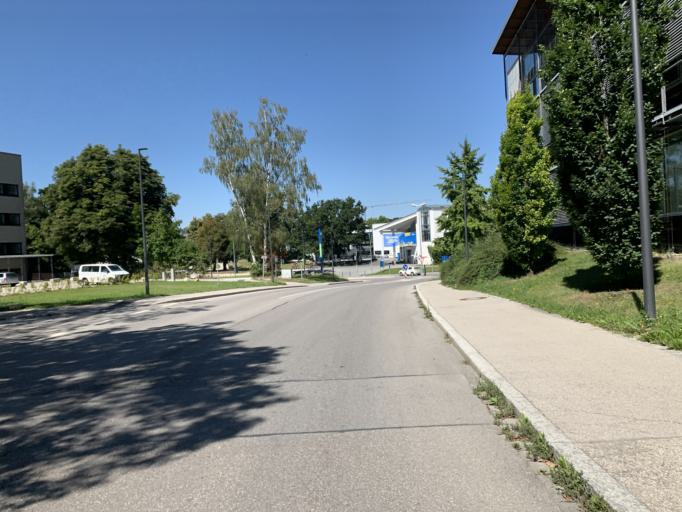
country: DE
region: Bavaria
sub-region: Upper Bavaria
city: Freising
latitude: 48.3972
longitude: 11.7241
